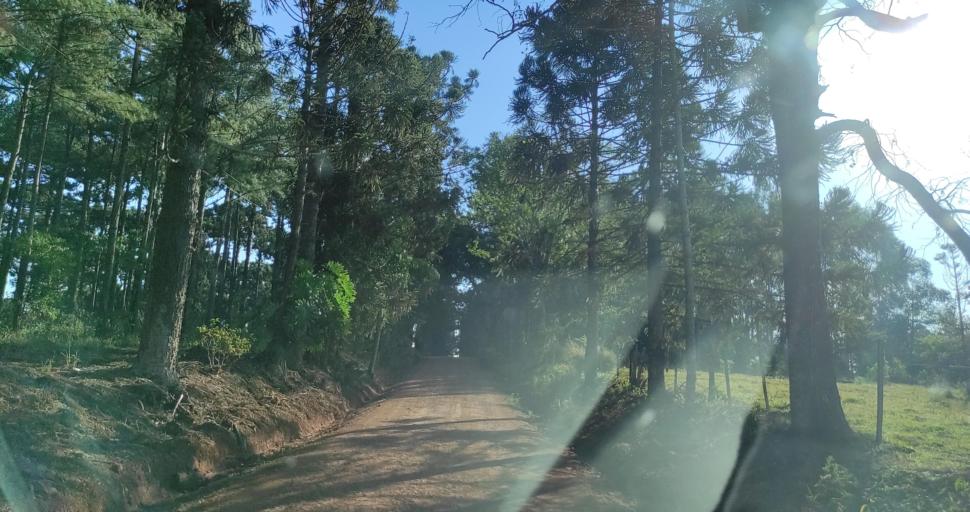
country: AR
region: Misiones
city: Capiovi
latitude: -26.8736
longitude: -55.1120
